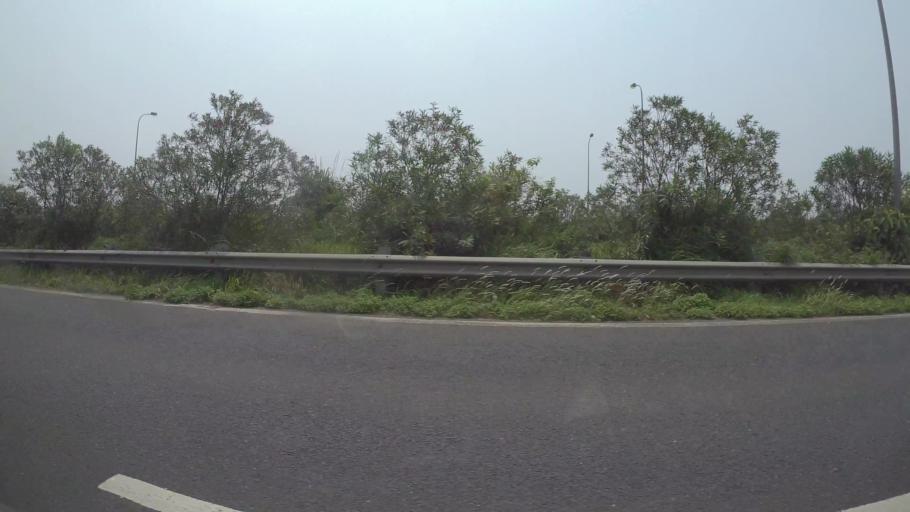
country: VN
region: Ha Noi
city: Quoc Oai
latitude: 20.9965
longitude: 105.5920
